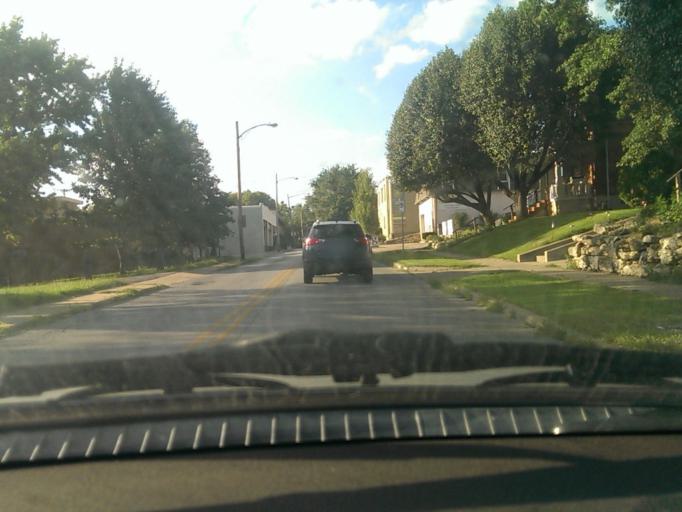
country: US
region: Kansas
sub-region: Johnson County
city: Westwood
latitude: 39.0455
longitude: -94.6073
